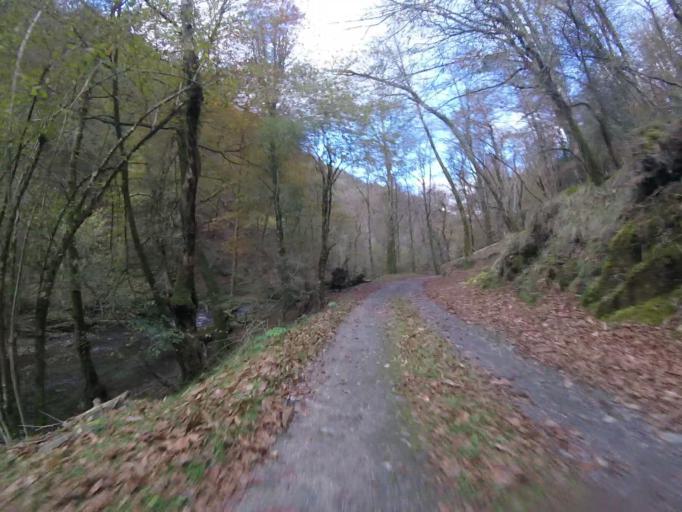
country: ES
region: Navarre
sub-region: Provincia de Navarra
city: Goizueta
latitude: 43.1973
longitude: -1.8048
